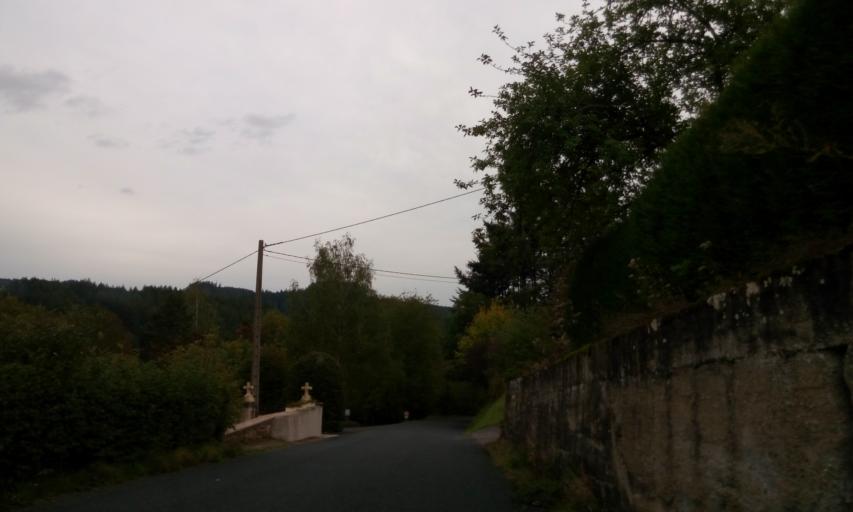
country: FR
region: Rhone-Alpes
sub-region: Departement du Rhone
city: Cublize
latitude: 46.0758
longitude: 4.3892
